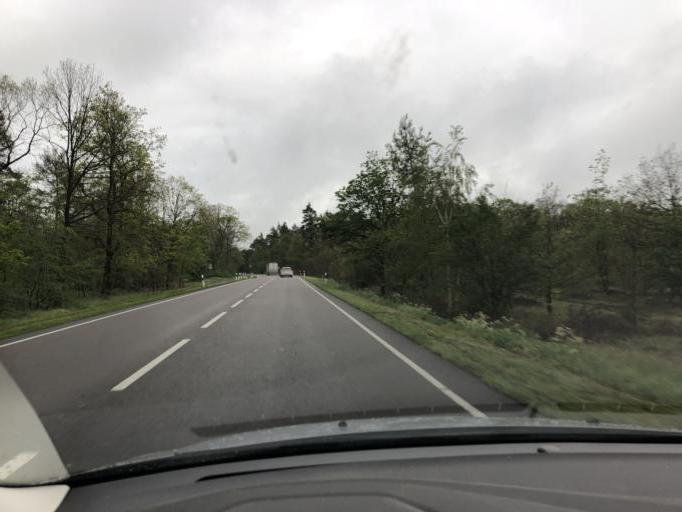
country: DE
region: Saxony-Anhalt
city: Raguhn
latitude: 51.7664
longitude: 12.2283
